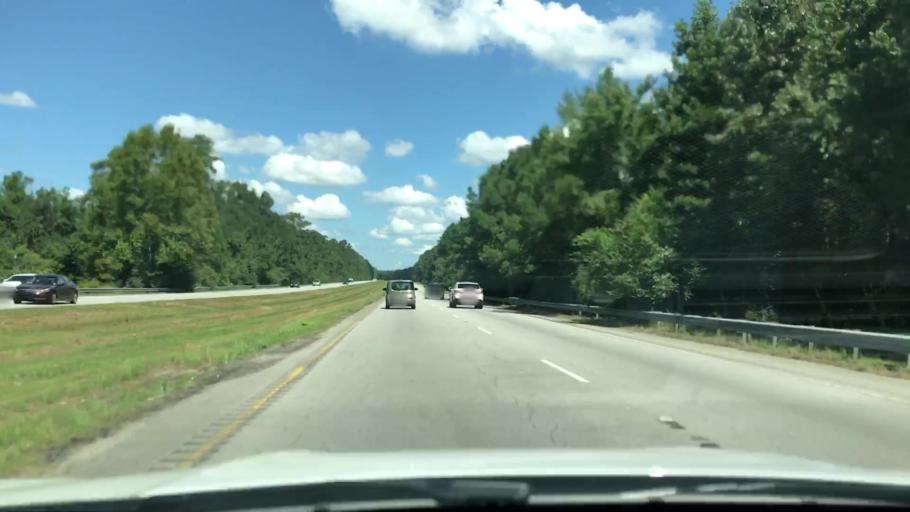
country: US
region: South Carolina
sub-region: Berkeley County
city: Hanahan
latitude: 32.9364
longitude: -79.9974
